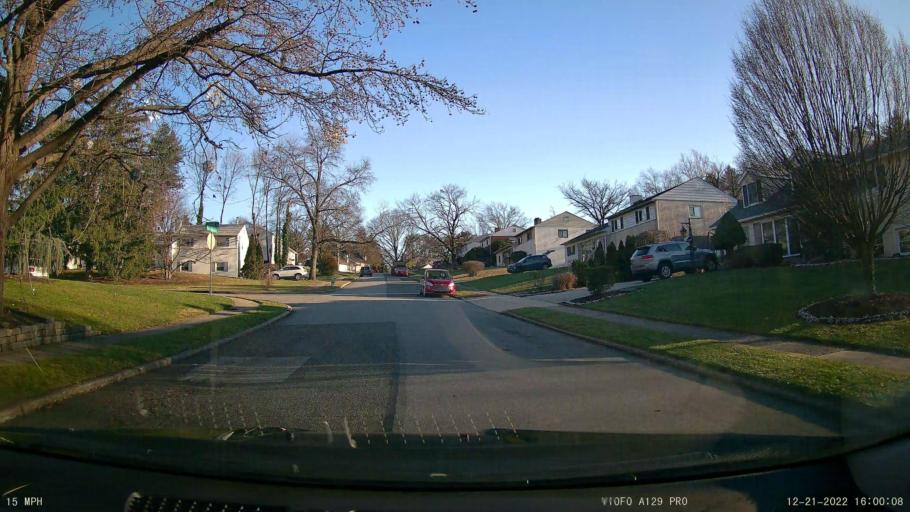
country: US
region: Pennsylvania
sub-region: Montgomery County
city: King of Prussia
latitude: 40.1038
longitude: -75.3798
